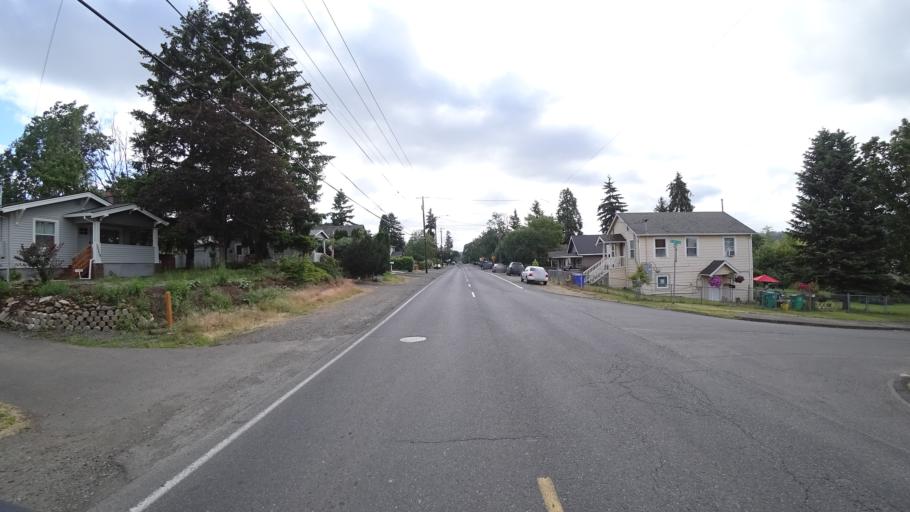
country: US
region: Oregon
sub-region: Multnomah County
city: Lents
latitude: 45.4826
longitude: -122.5573
